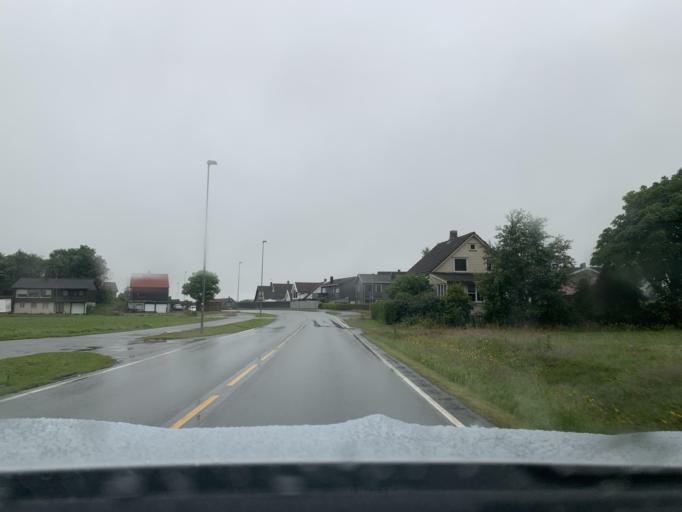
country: NO
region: Rogaland
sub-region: Time
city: Bryne
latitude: 58.7391
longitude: 5.6293
